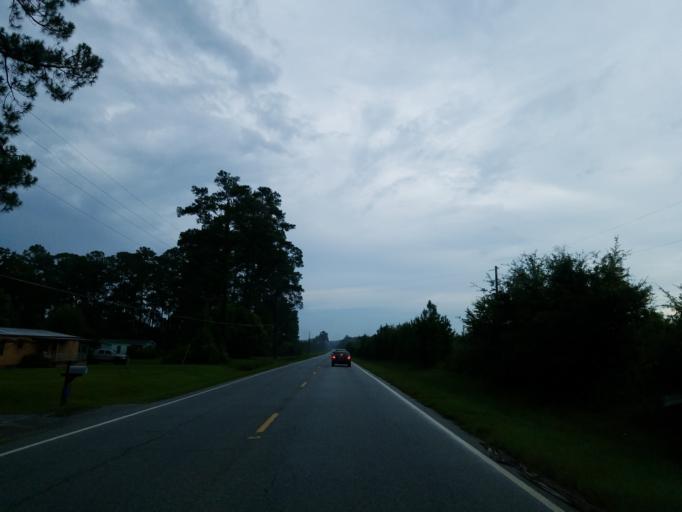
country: US
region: Georgia
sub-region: Berrien County
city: Ray City
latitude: 31.0599
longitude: -83.1547
